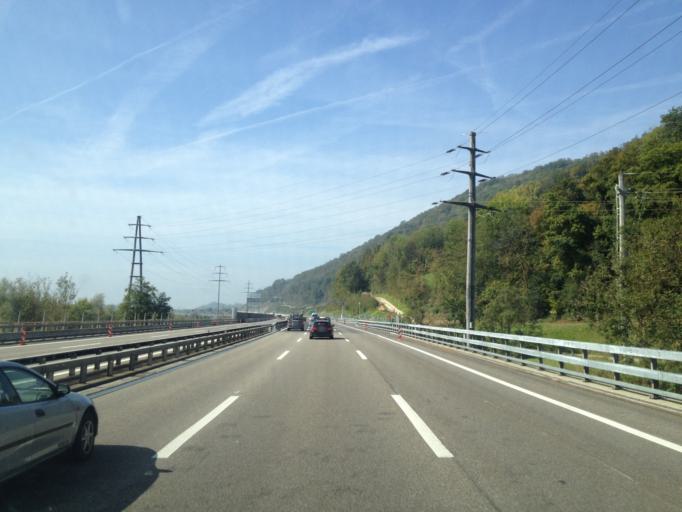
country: CH
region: Aargau
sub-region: Bezirk Zofingen
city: Rothrist
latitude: 47.3133
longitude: 7.8874
